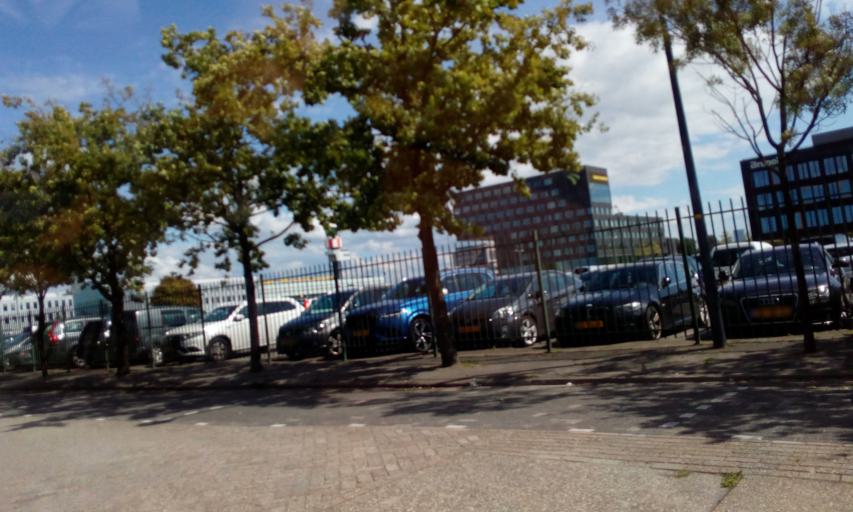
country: NL
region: South Holland
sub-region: Gemeente Schiedam
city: Schiedam
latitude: 51.9496
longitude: 4.4292
